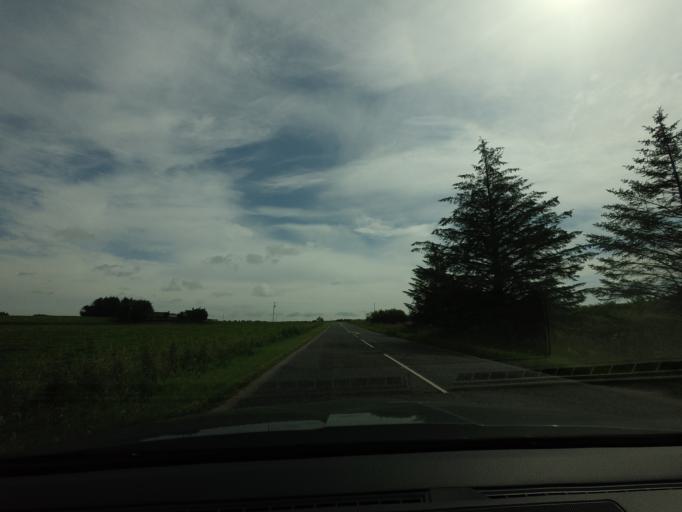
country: GB
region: Scotland
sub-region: Aberdeenshire
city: Rosehearty
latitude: 57.6005
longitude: -2.2519
